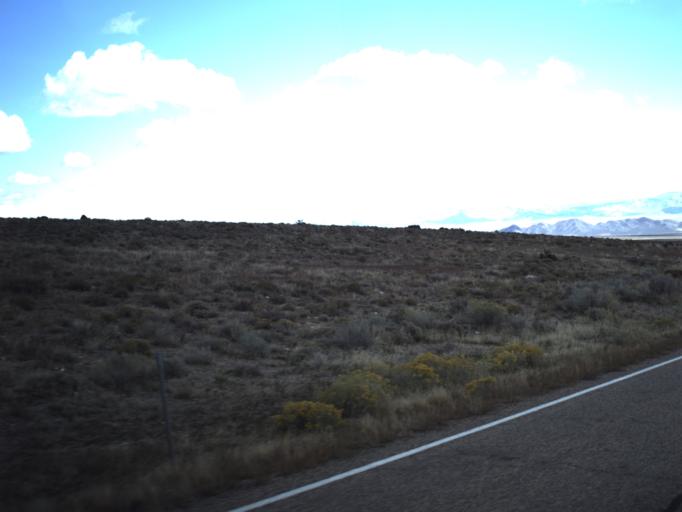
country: US
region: Utah
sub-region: Beaver County
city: Milford
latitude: 38.4573
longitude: -113.2258
